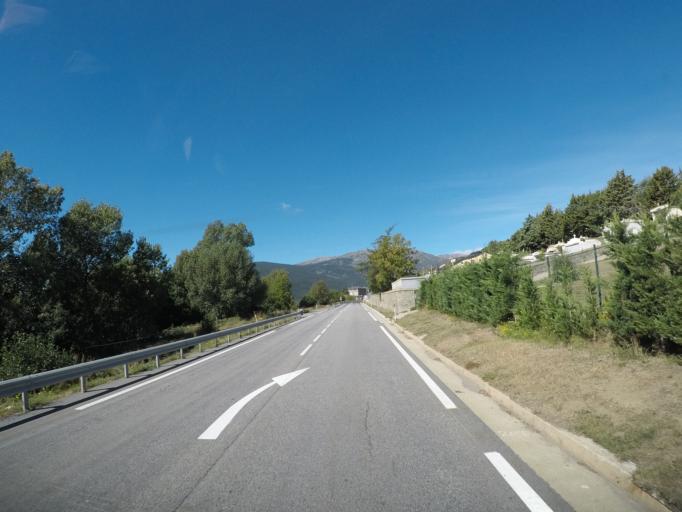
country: ES
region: Catalonia
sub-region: Provincia de Girona
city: Puigcerda
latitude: 42.4580
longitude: 1.9233
